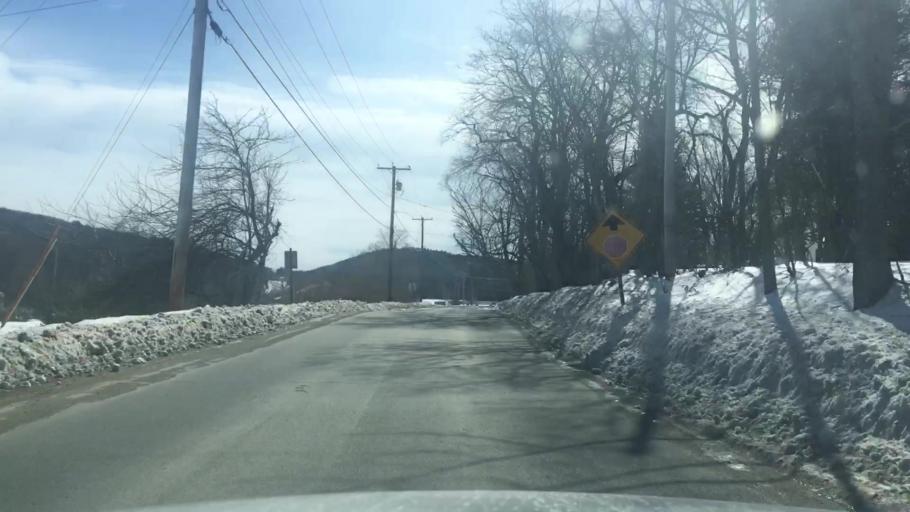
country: US
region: Maine
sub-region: Penobscot County
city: Holden
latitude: 44.7392
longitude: -68.6287
